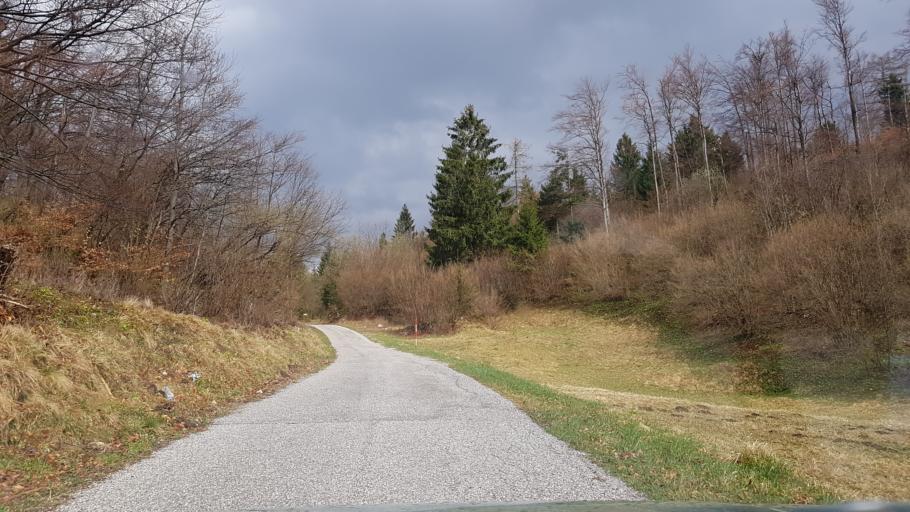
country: SI
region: Cerkno
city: Cerkno
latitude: 46.1364
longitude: 13.8788
